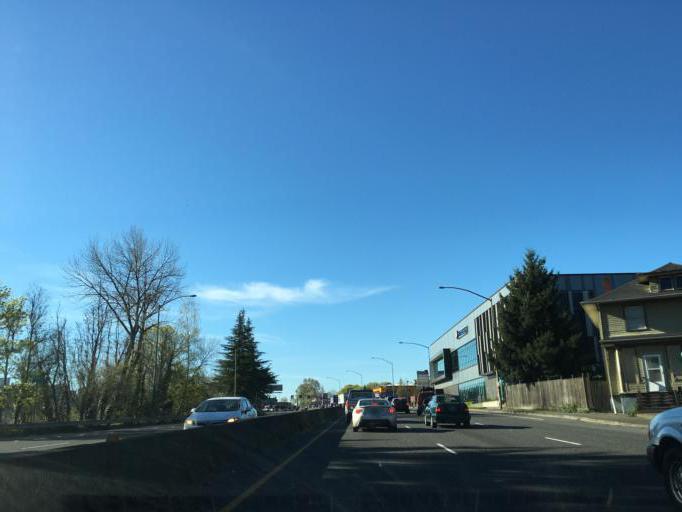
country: US
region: Oregon
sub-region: Multnomah County
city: Portland
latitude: 45.4885
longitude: -122.6517
